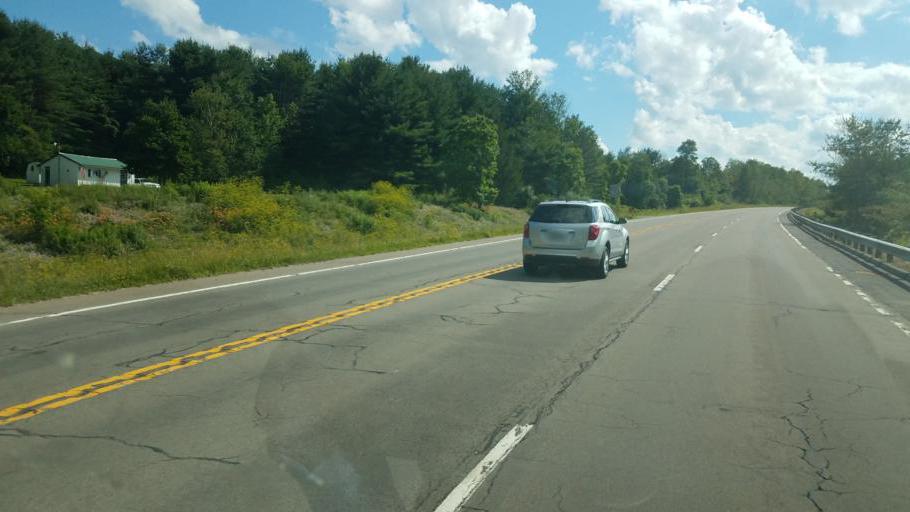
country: US
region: New York
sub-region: Steuben County
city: Bath
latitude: 42.3773
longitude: -77.2717
